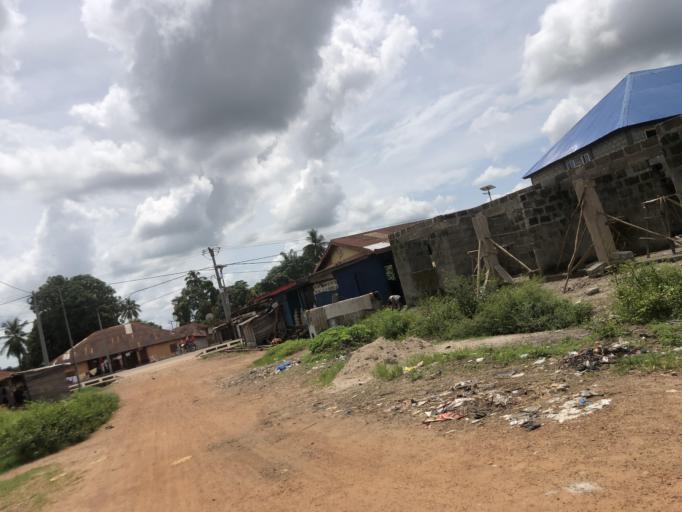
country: SL
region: Northern Province
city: Makeni
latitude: 8.8793
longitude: -12.0499
